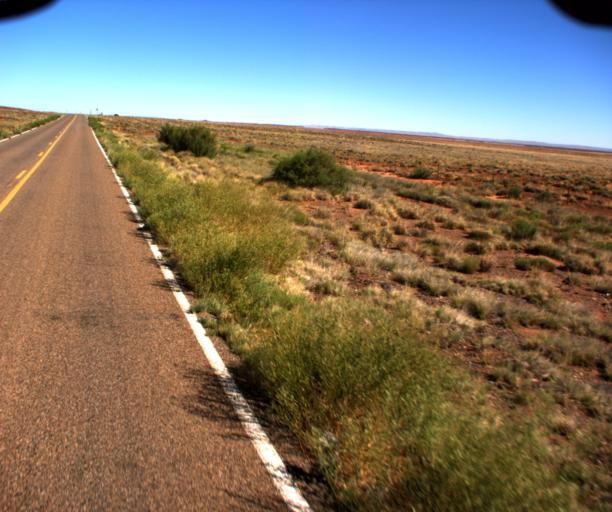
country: US
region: Arizona
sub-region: Coconino County
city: LeChee
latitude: 35.1687
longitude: -110.9158
